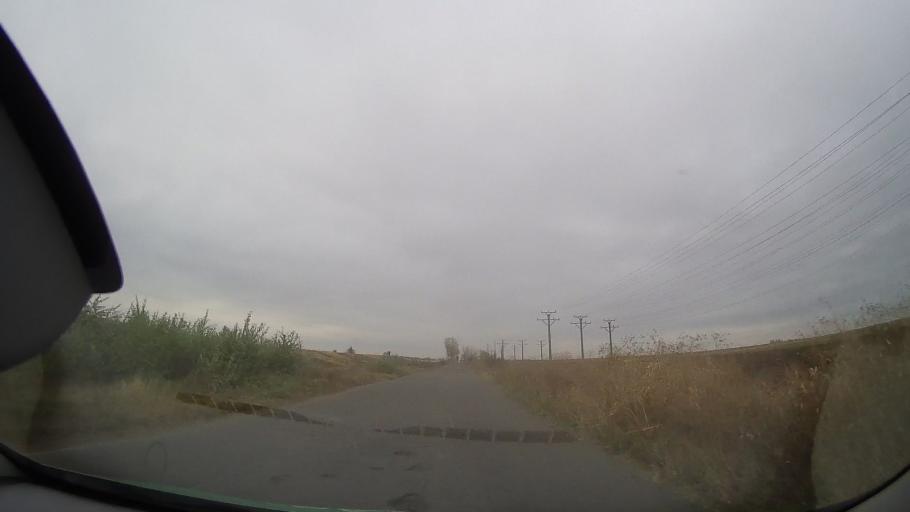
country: RO
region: Braila
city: Dudesti
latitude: 44.9104
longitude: 27.4308
